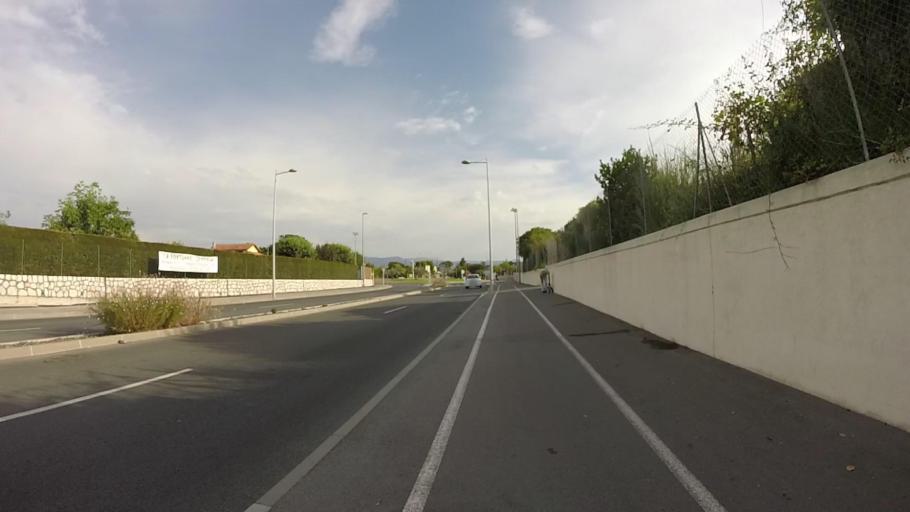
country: FR
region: Provence-Alpes-Cote d'Azur
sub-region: Departement des Alpes-Maritimes
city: Biot
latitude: 43.6023
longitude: 7.1127
